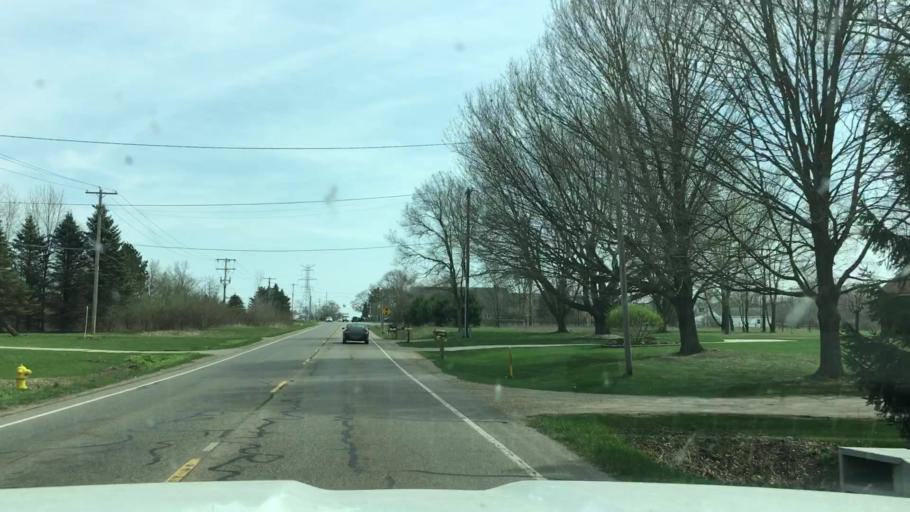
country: US
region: Michigan
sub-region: Ottawa County
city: Hudsonville
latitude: 42.8881
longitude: -85.9016
